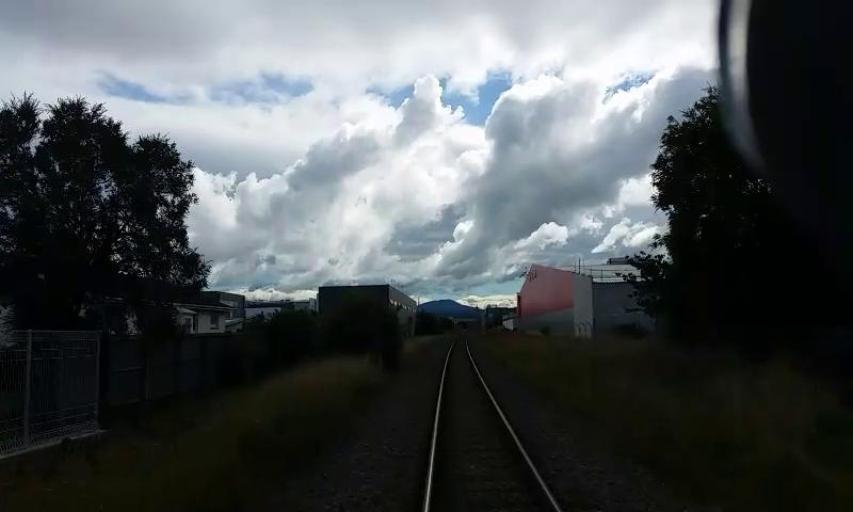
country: NZ
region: Canterbury
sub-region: Waimakariri District
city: Woodend
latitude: -43.3053
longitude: 172.5988
